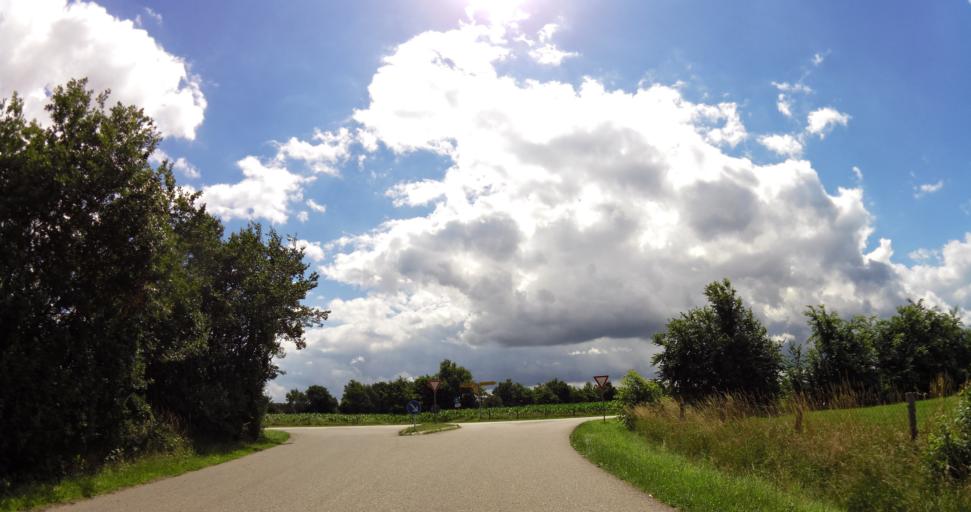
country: DE
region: Schleswig-Holstein
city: Hummelfeld
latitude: 54.4907
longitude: 9.7296
